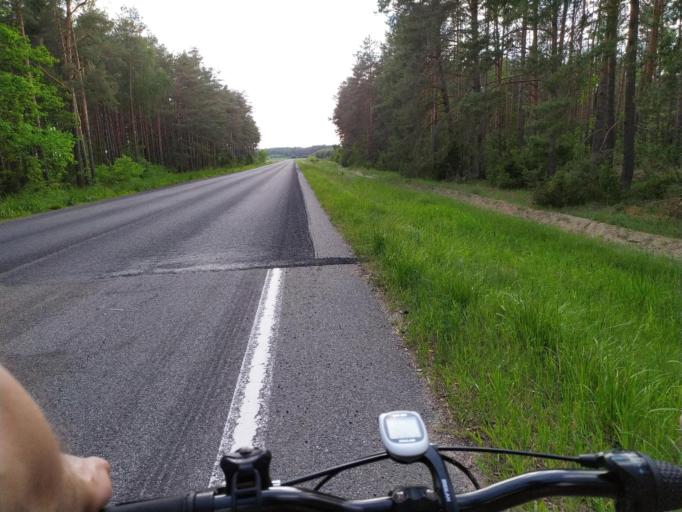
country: BY
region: Brest
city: Zhabinka
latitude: 52.3980
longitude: 24.0493
